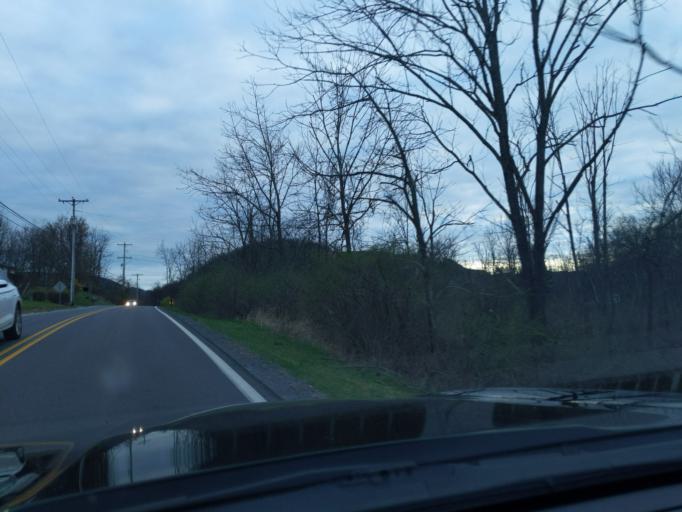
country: US
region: Pennsylvania
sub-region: Blair County
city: Lakemont
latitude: 40.4546
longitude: -78.3504
